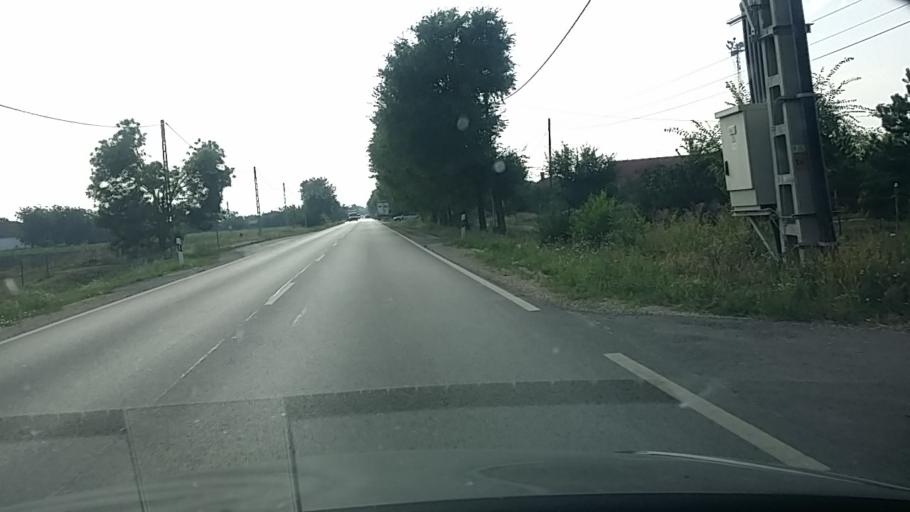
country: HU
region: Bekes
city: Szarvas
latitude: 46.8488
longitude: 20.5943
